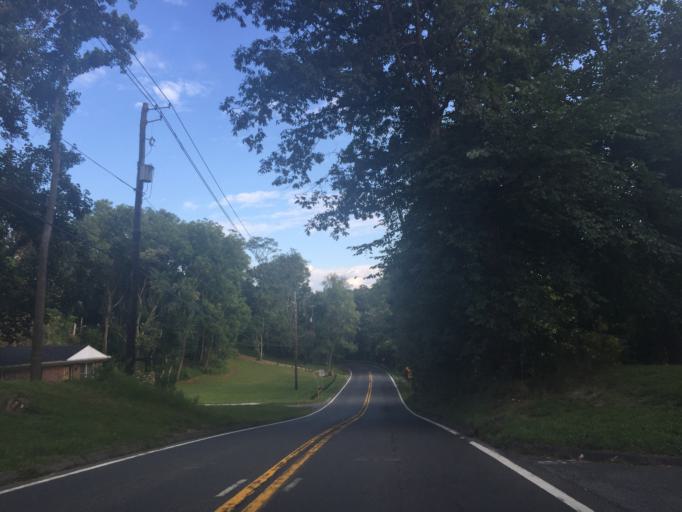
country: US
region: Maryland
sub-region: Montgomery County
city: Montgomery Village
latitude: 39.2066
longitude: -77.1683
